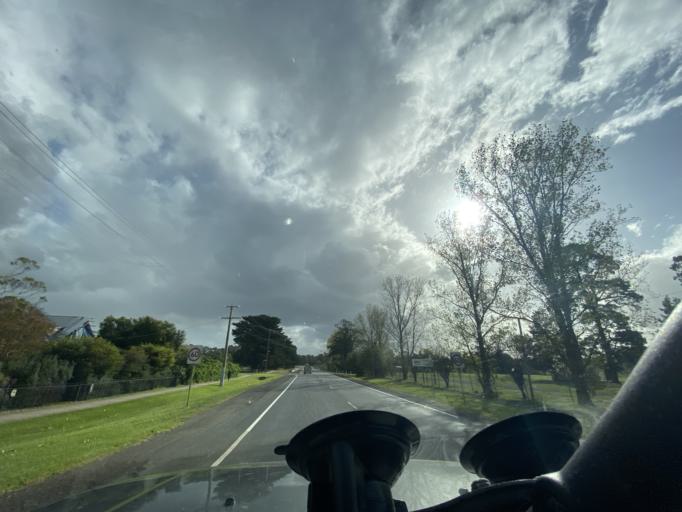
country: AU
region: Victoria
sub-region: Whittlesea
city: Whittlesea
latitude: -37.5108
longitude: 145.1294
